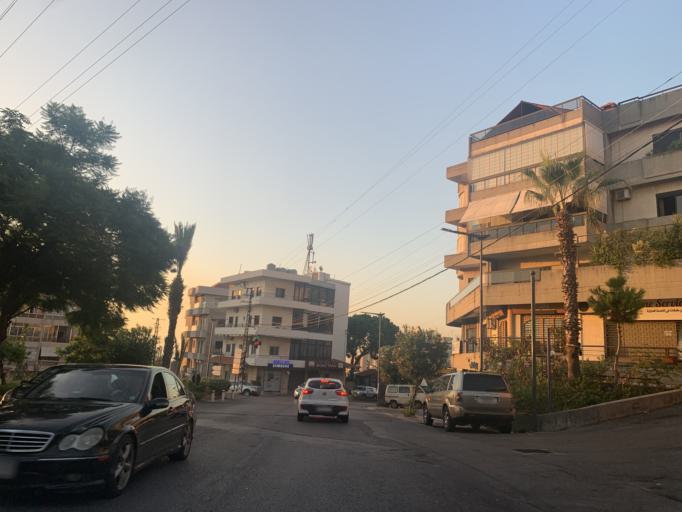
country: LB
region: Mont-Liban
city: Djounie
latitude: 33.9634
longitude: 35.6242
